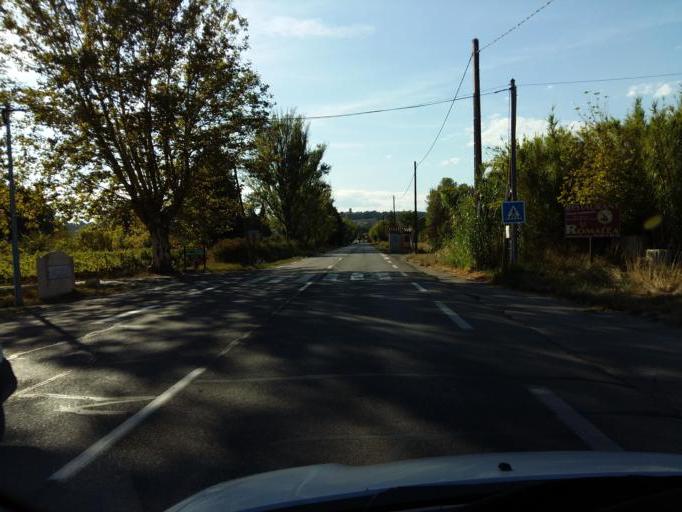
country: FR
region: Provence-Alpes-Cote d'Azur
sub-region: Departement du Vaucluse
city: Chateauneuf-de-Gadagne
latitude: 43.9252
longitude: 4.9608
